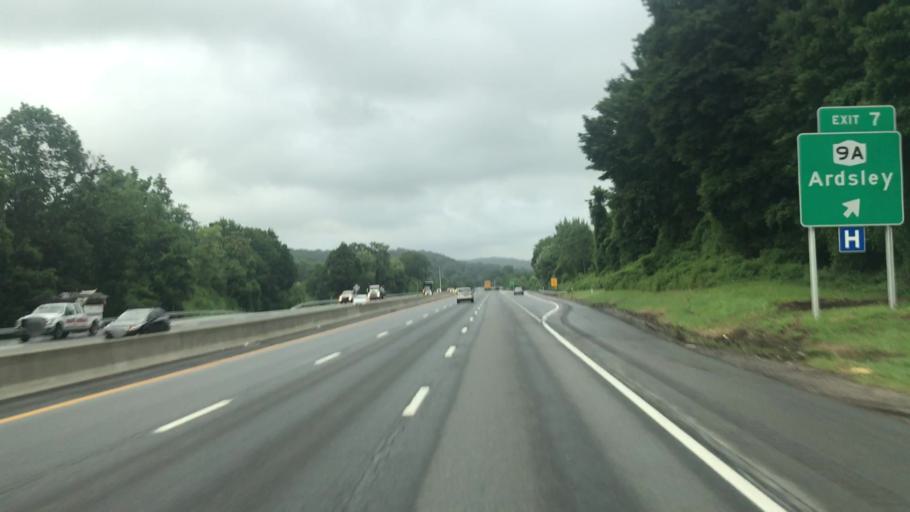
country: US
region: New York
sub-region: Westchester County
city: Ardsley
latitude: 41.0041
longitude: -73.8522
